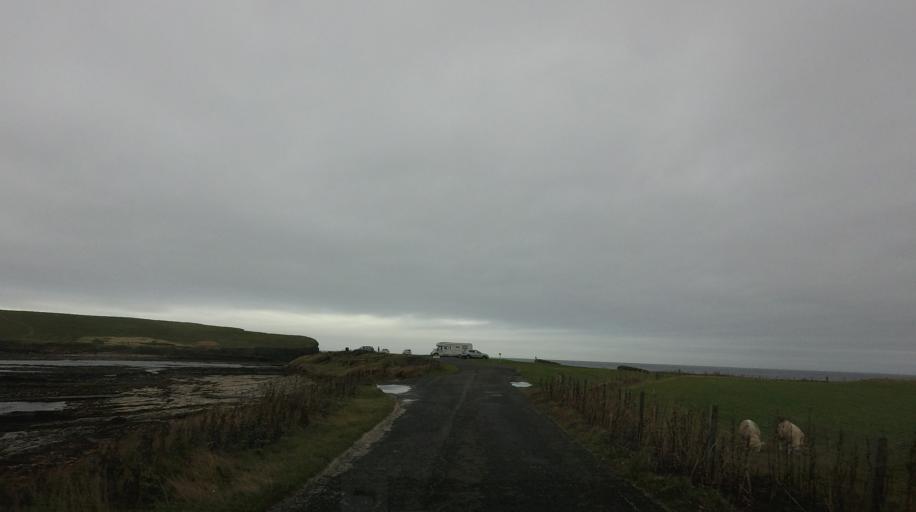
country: GB
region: Scotland
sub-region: Orkney Islands
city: Stromness
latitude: 59.1345
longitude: -3.3235
